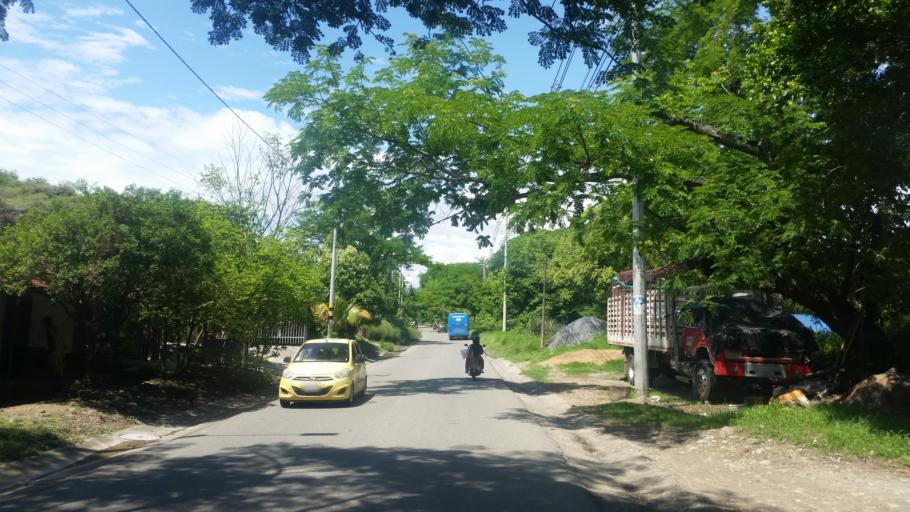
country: CO
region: Huila
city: Neiva
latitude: 2.9852
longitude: -75.2775
